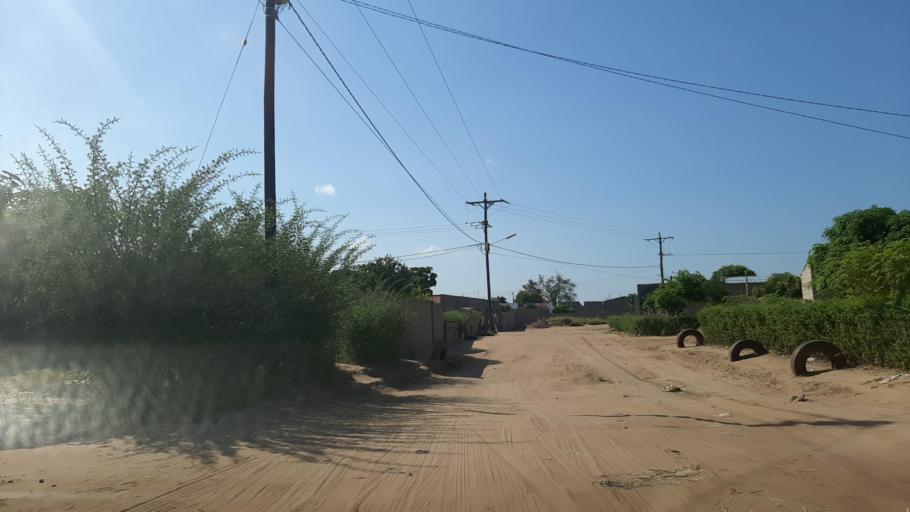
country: MZ
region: Maputo
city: Matola
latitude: -25.8054
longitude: 32.4911
